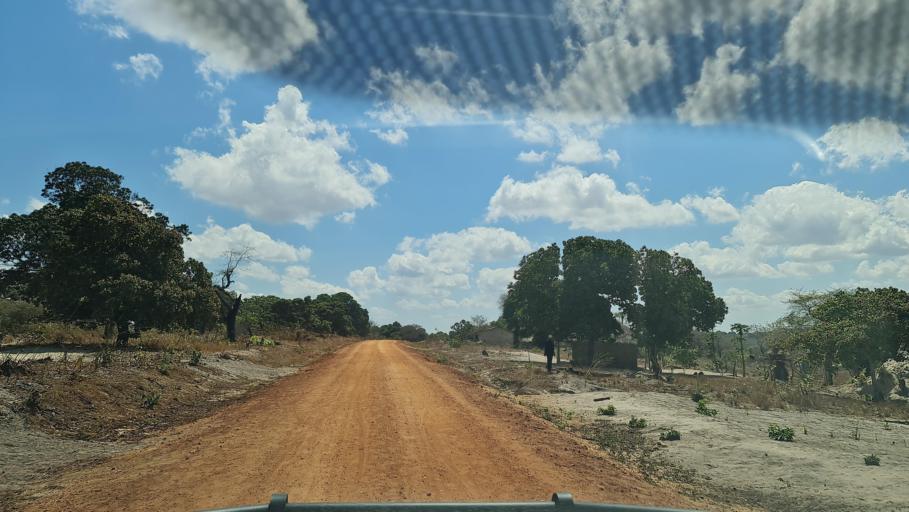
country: MZ
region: Nampula
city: Nacala
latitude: -14.1708
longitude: 40.2458
